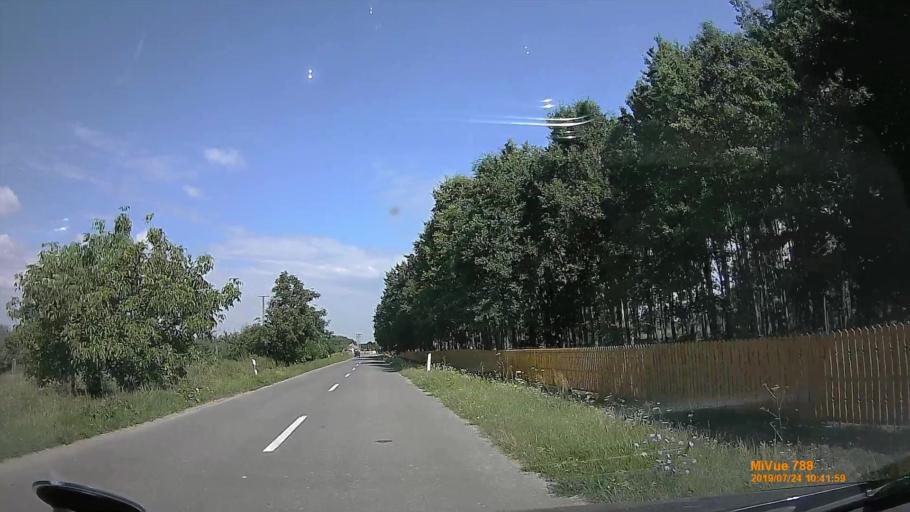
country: HU
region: Szabolcs-Szatmar-Bereg
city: Tarpa
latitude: 48.1940
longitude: 22.5475
